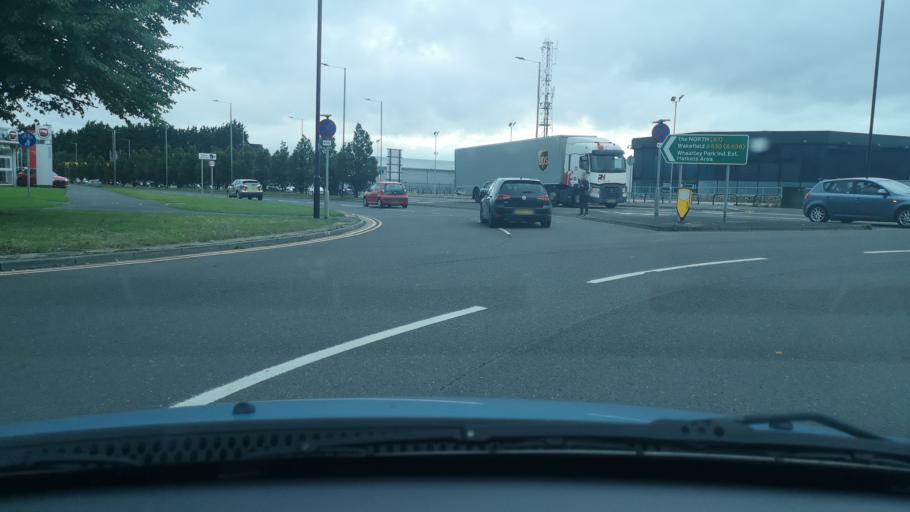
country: GB
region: England
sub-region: Doncaster
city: Kirk Sandall
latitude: 53.5478
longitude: -1.0884
